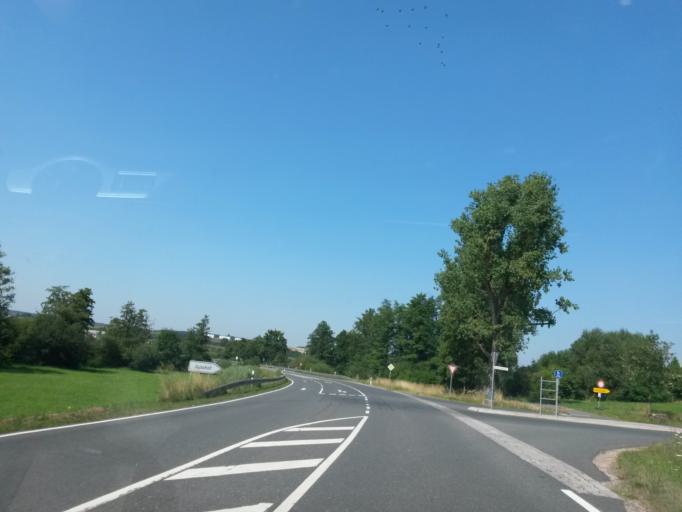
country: DE
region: Bavaria
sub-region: Upper Franconia
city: Schlusselfeld
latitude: 49.7382
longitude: 10.6333
